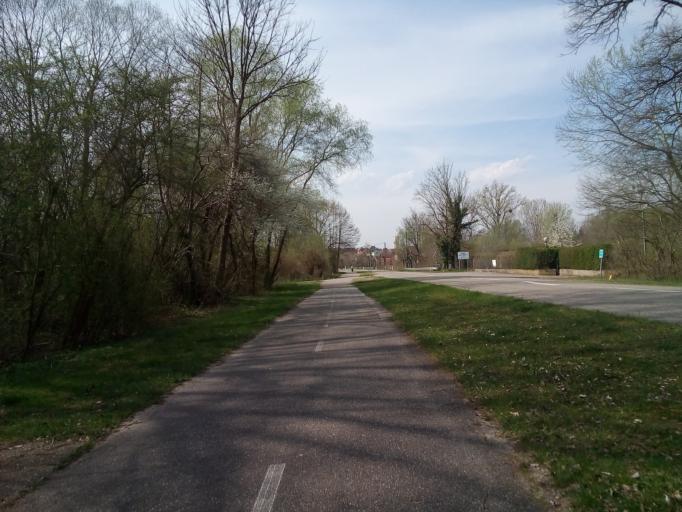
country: FR
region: Alsace
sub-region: Departement du Bas-Rhin
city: Seltz
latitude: 48.8909
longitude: 8.1164
